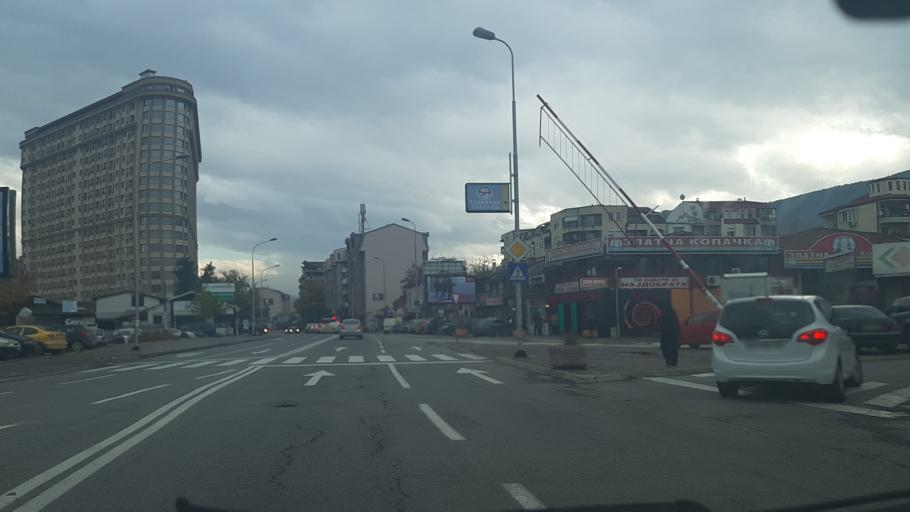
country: MK
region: Karpos
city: Skopje
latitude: 41.9869
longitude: 21.4371
